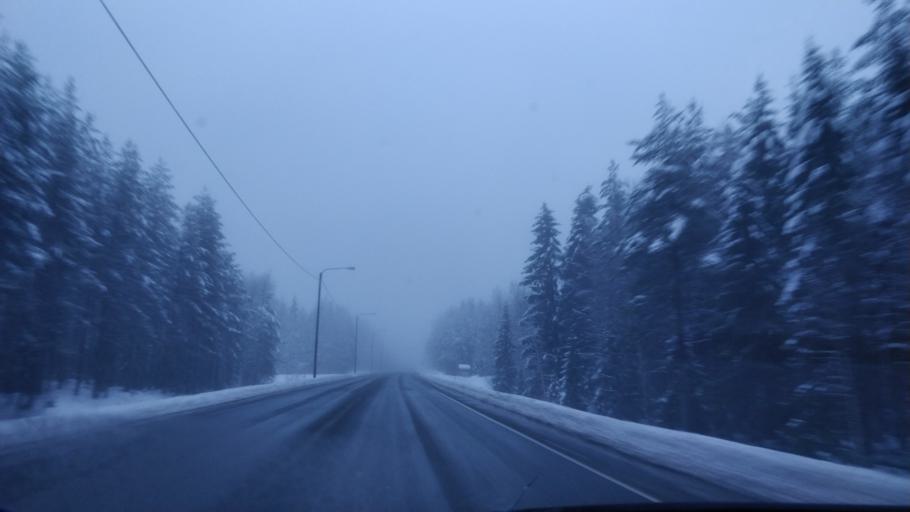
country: FI
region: Lapland
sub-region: Kemi-Tornio
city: Tervola
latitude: 66.1326
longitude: 24.9060
